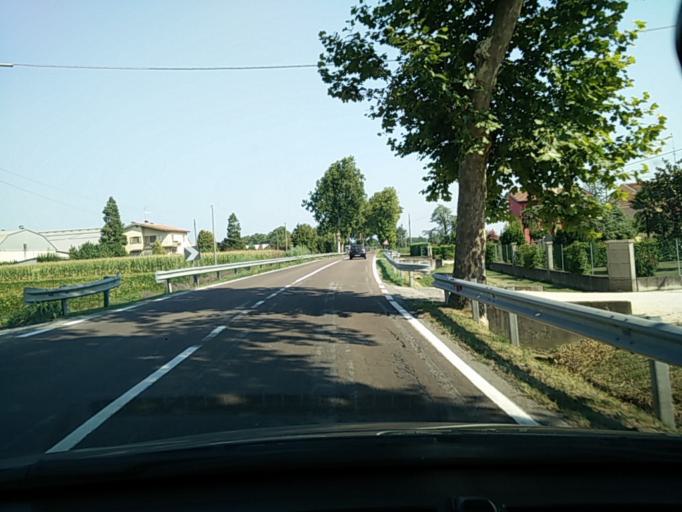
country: IT
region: Veneto
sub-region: Provincia di Venezia
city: San Giorgio di Livenza
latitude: 45.6490
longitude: 12.7741
